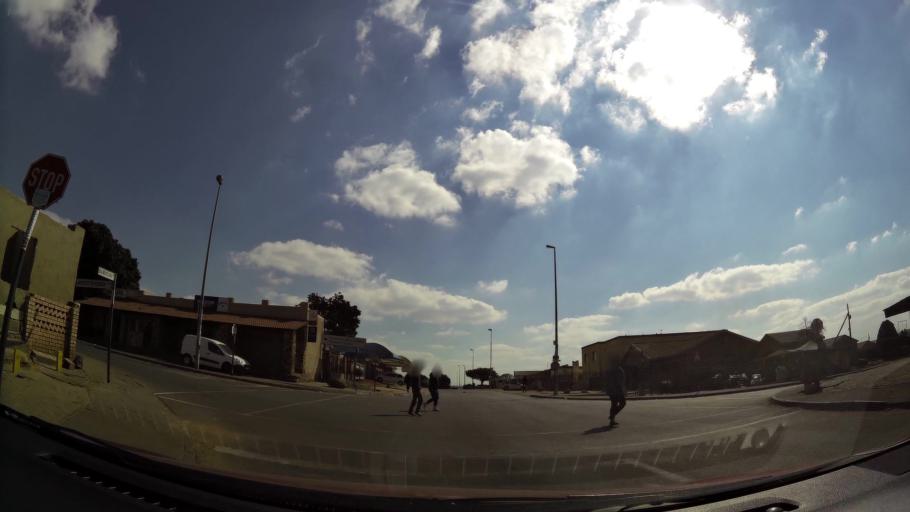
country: ZA
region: Gauteng
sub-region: Ekurhuleni Metropolitan Municipality
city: Tembisa
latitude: -26.0160
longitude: 28.1976
